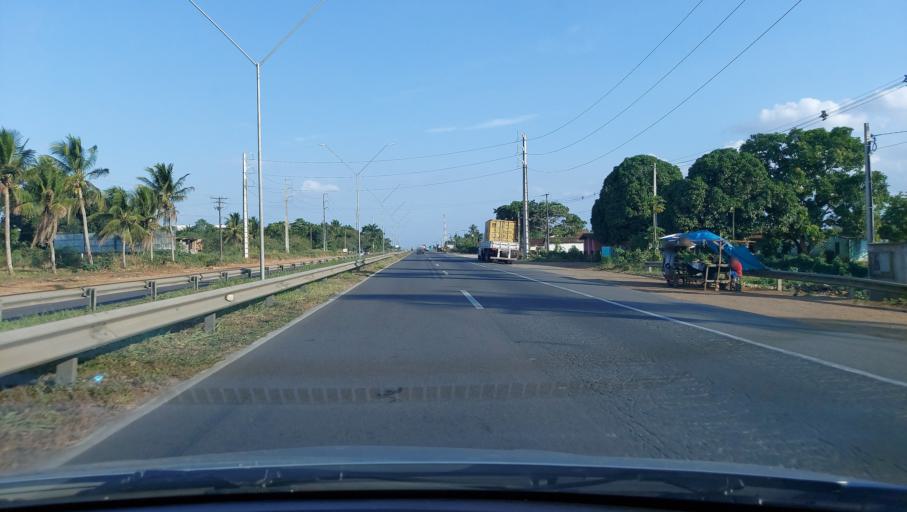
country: BR
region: Bahia
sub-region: Conceicao Do Jacuipe
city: Conceicao do Jacuipe
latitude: -12.3701
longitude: -38.8128
